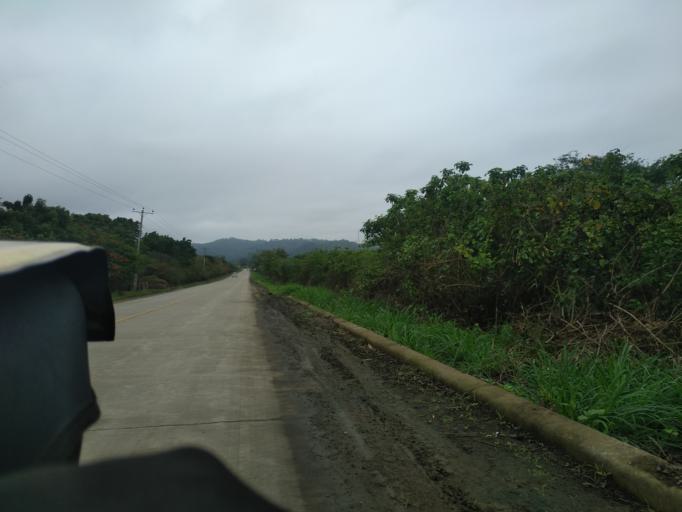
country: EC
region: Manabi
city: Jipijapa
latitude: -1.6576
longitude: -80.8188
